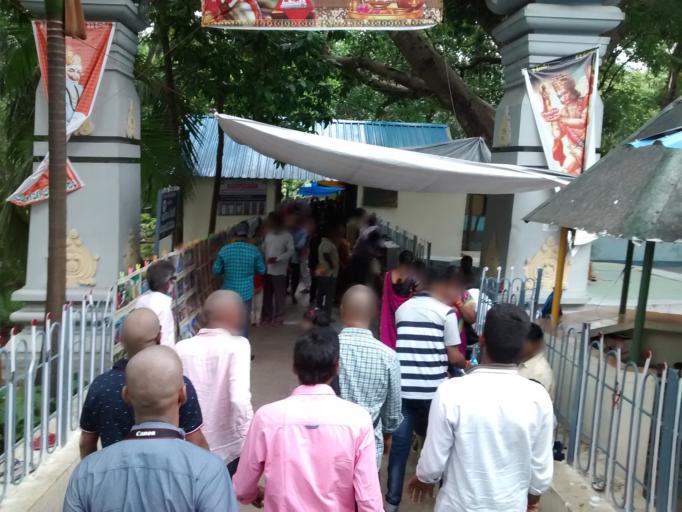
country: IN
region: Andhra Pradesh
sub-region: Chittoor
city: Tirumala
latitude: 13.7062
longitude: 79.3412
